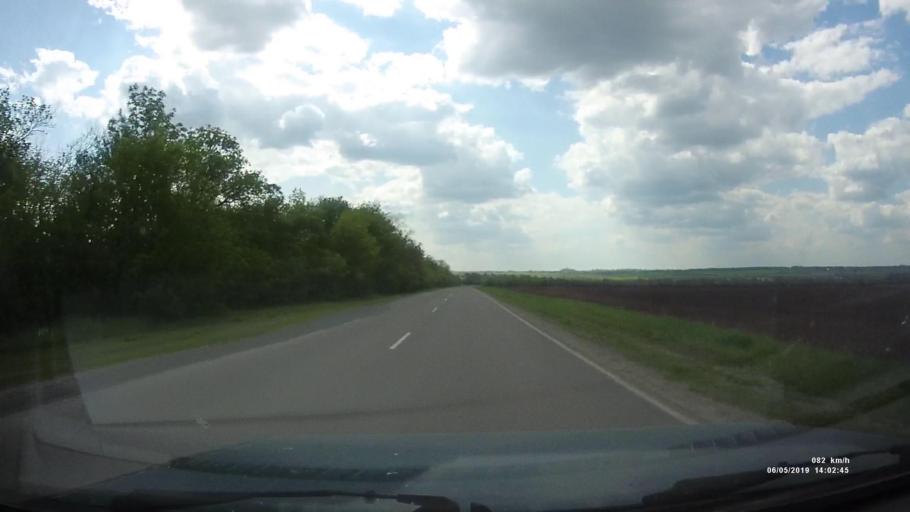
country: RU
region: Rostov
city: Shakhty
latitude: 47.6816
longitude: 40.3581
